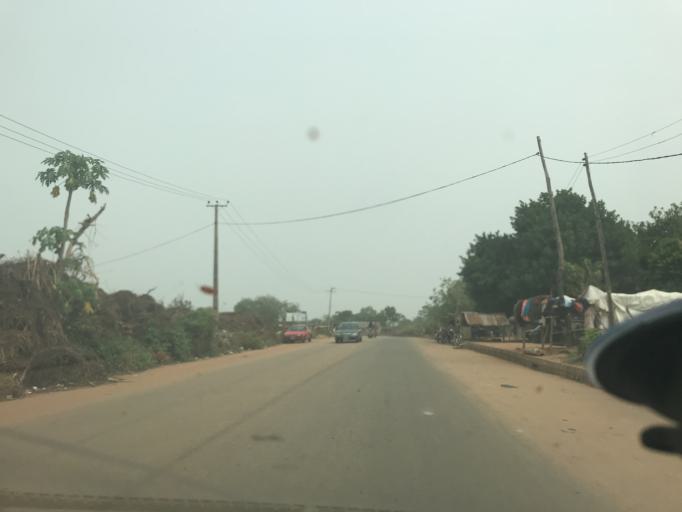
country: NG
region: Ogun
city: Ilaro
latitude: 6.8948
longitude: 3.0186
